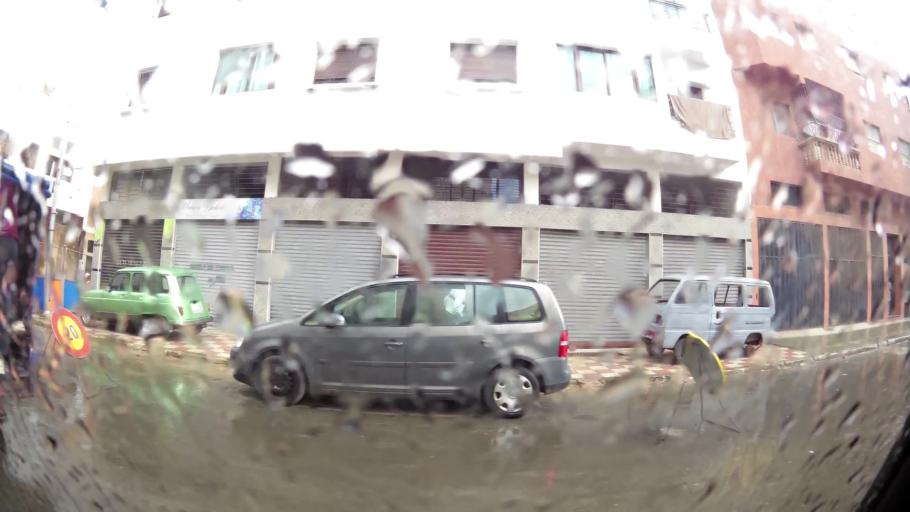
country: MA
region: Grand Casablanca
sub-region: Casablanca
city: Casablanca
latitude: 33.5627
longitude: -7.6921
